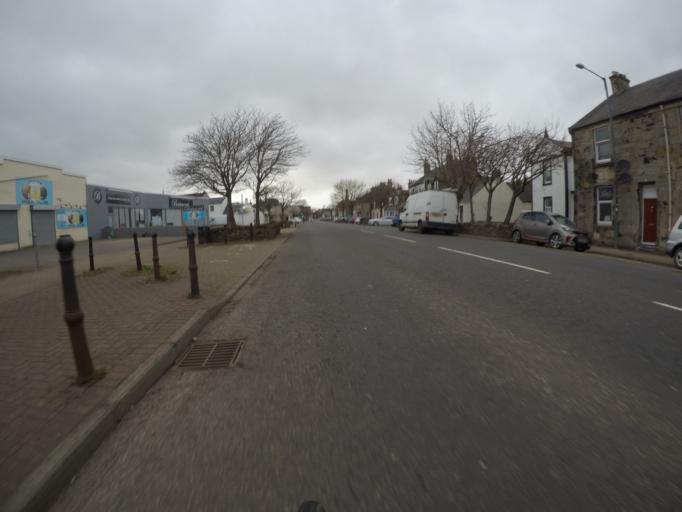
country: GB
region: Scotland
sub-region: North Ayrshire
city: Irvine
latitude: 55.6134
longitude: -4.6604
